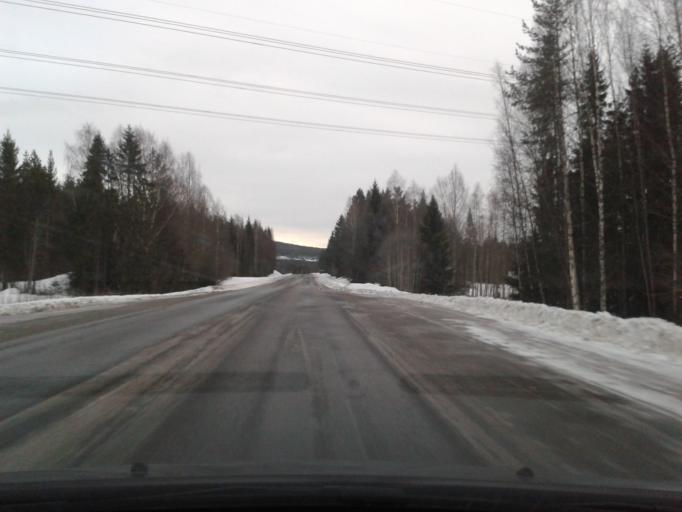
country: SE
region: Vaesternorrland
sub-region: Solleftea Kommun
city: Solleftea
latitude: 63.2966
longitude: 17.2143
